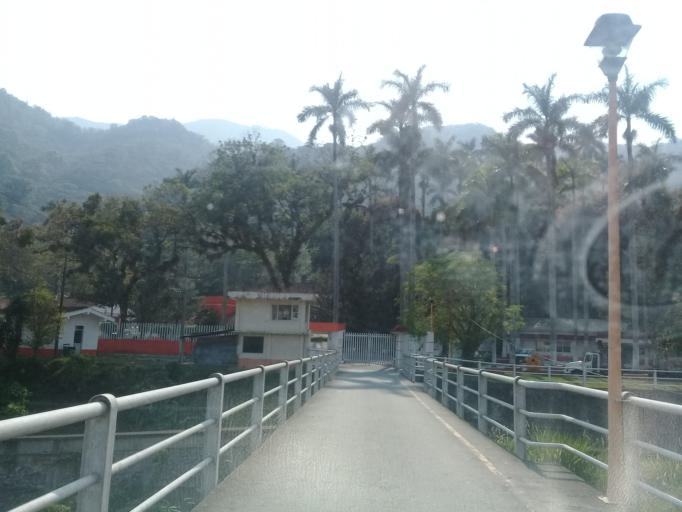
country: MX
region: Veracruz
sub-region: Ixtaczoquitlan
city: Campo Chico
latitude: 18.8366
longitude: -97.0334
